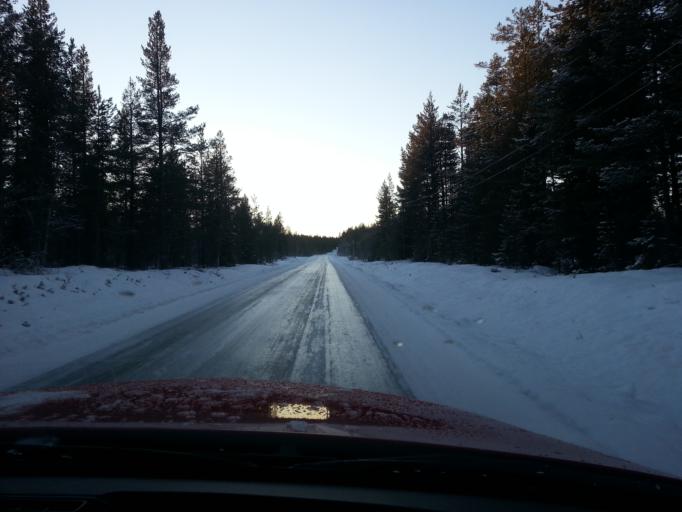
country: SE
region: Jaemtland
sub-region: Harjedalens Kommun
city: Sveg
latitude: 62.3642
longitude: 13.4626
